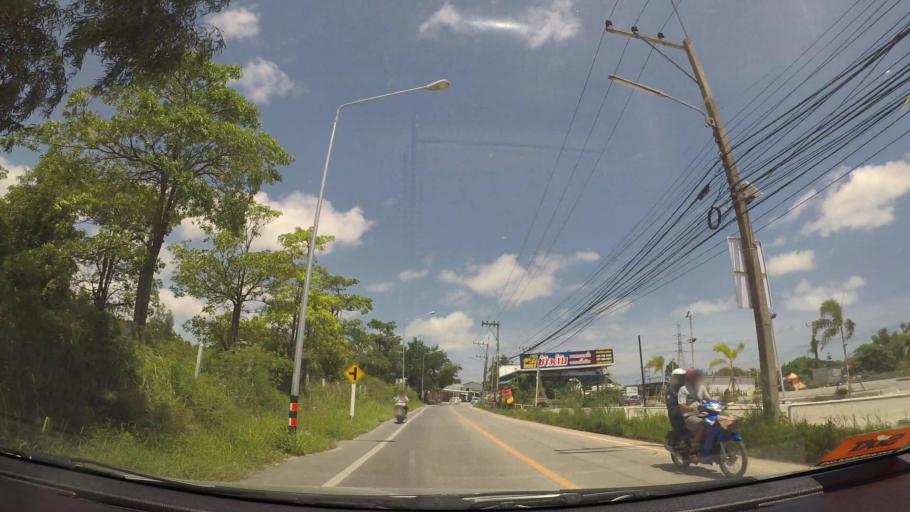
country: TH
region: Rayong
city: Rayong
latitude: 12.6921
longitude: 101.2689
